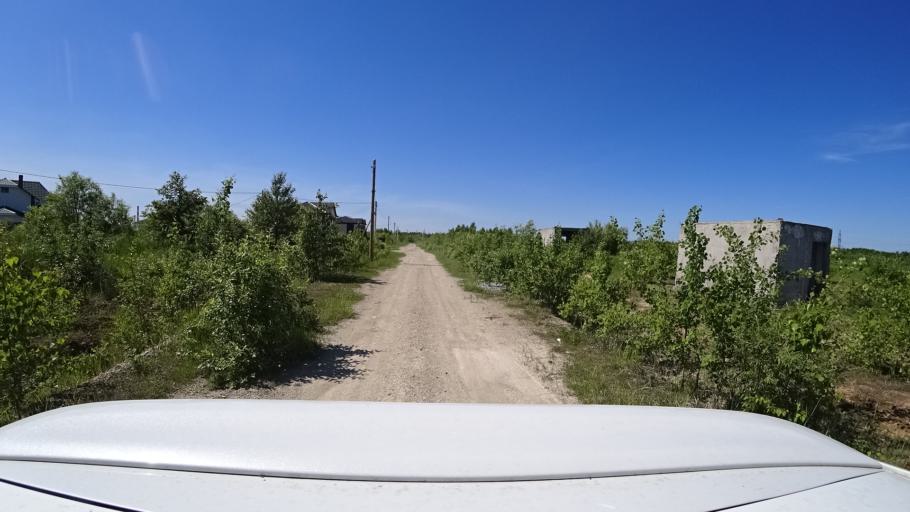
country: RU
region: Khabarovsk Krai
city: Topolevo
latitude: 48.5652
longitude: 135.1932
